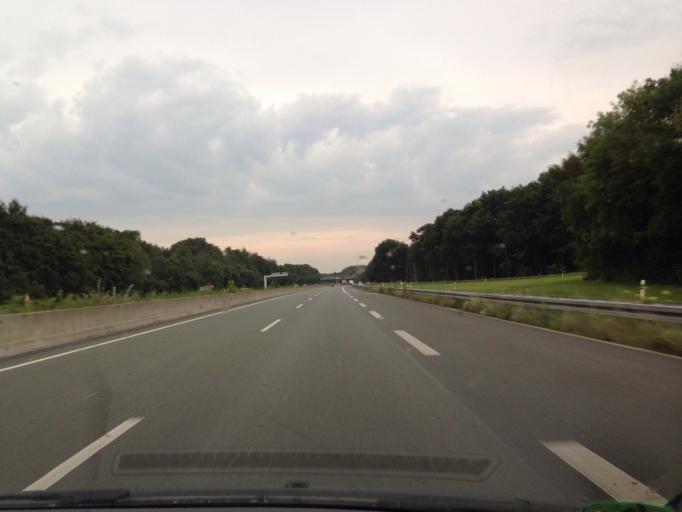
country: DE
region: North Rhine-Westphalia
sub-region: Regierungsbezirk Munster
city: Muenster
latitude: 51.9154
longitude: 7.5621
